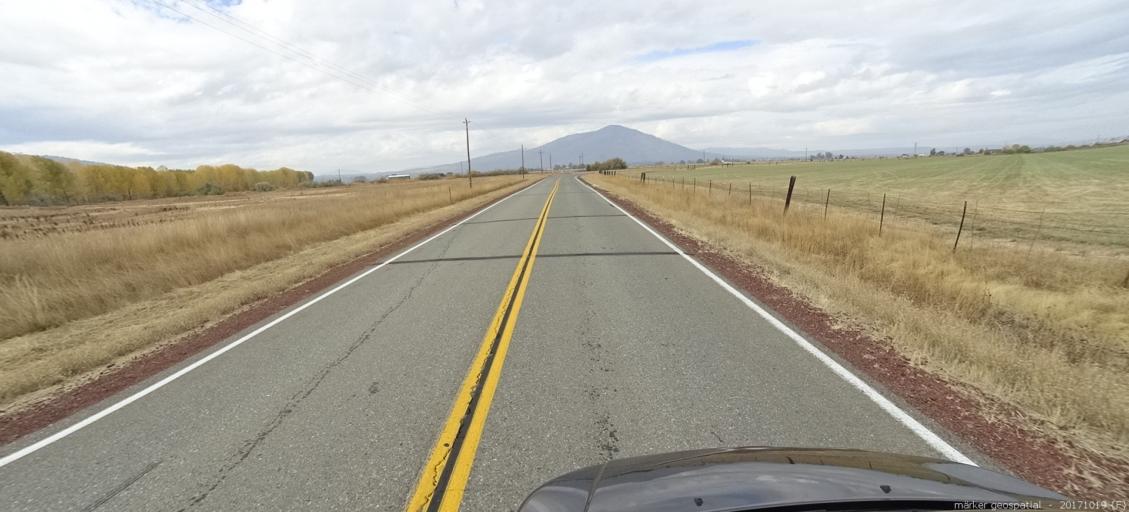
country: US
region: California
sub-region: Shasta County
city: Burney
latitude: 41.0523
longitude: -121.4573
